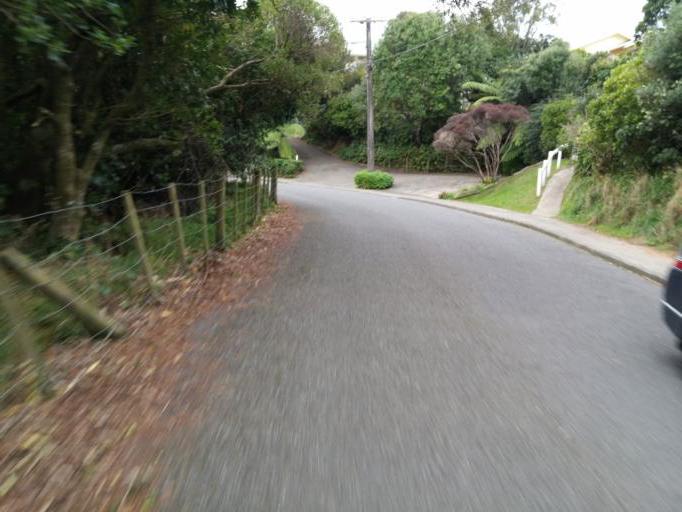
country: NZ
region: Wellington
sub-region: Wellington City
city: Kelburn
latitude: -41.2946
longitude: 174.7531
